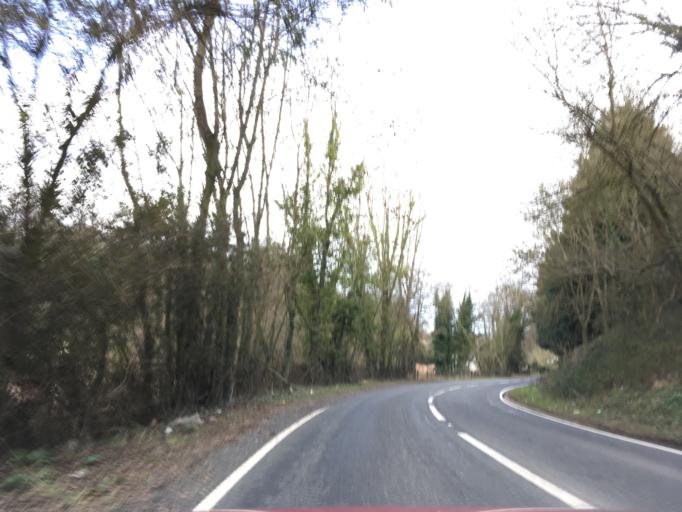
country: GB
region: England
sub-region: Gloucestershire
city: Cinderford
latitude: 51.8243
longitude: -2.4588
